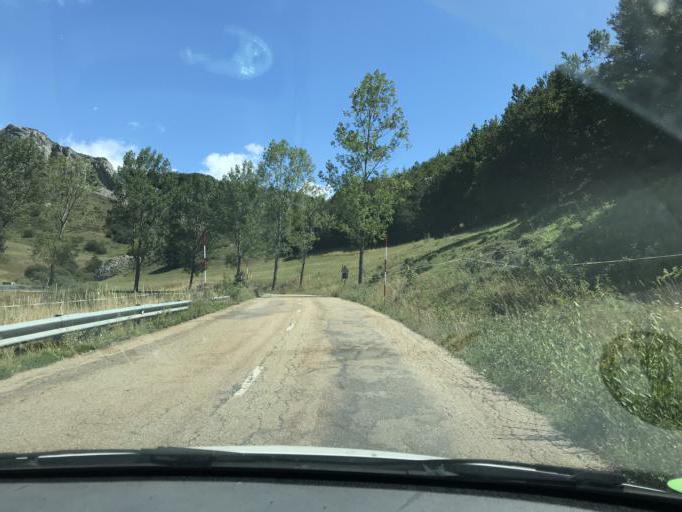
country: ES
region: Castille and Leon
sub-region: Provincia de Palencia
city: Polentinos
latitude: 43.0308
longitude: -4.4586
